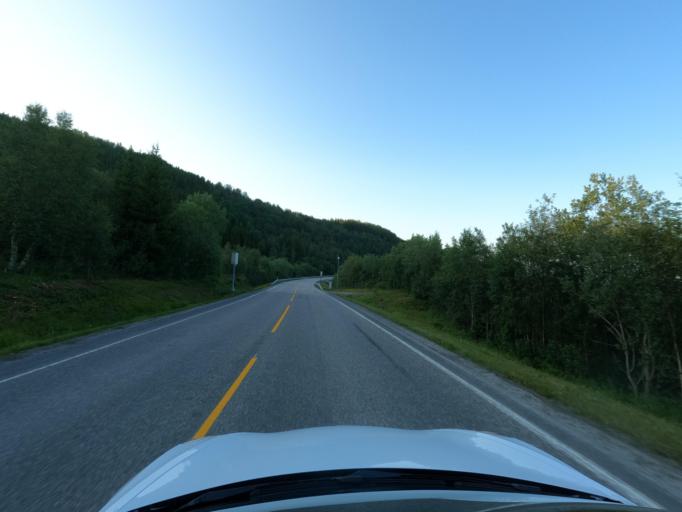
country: NO
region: Troms
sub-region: Harstad
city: Harstad
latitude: 68.7271
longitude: 16.5408
